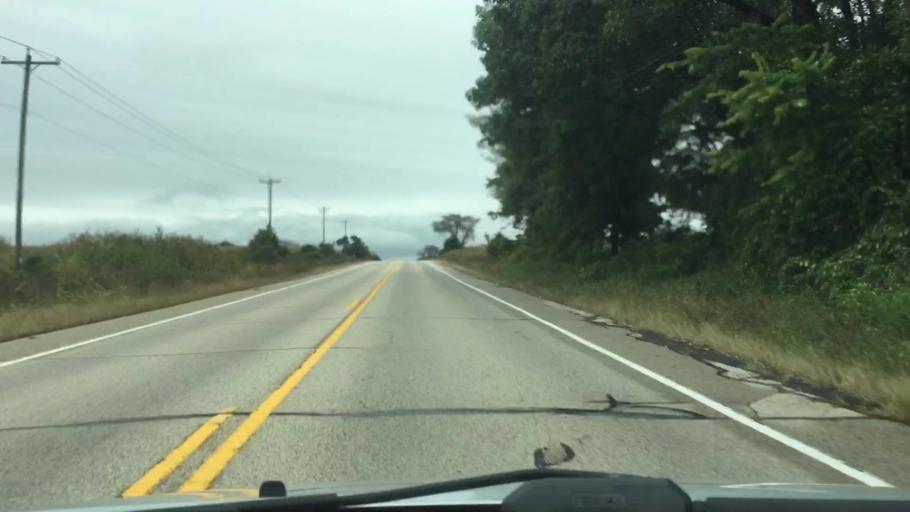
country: US
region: Wisconsin
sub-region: Jefferson County
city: Palmyra
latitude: 42.8113
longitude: -88.5625
